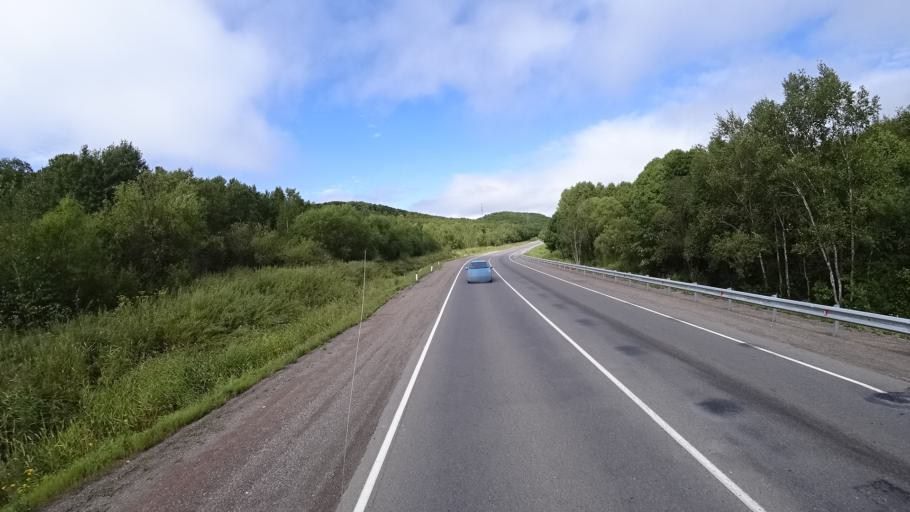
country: RU
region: Primorskiy
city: Lyalichi
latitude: 44.1160
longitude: 132.4192
